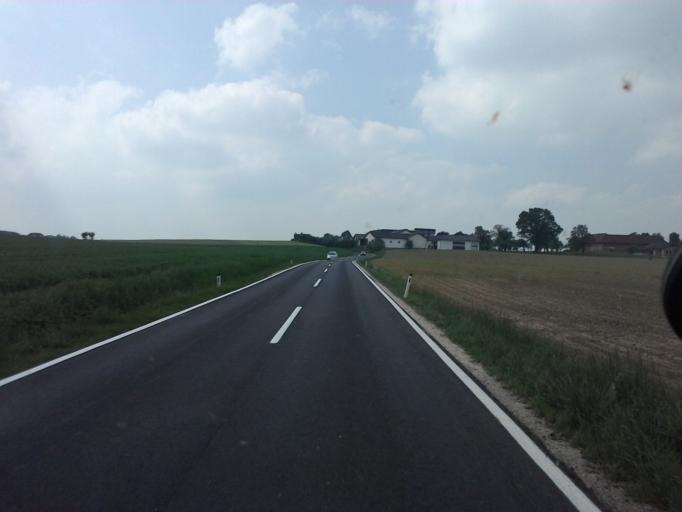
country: AT
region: Upper Austria
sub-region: Wels-Land
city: Sattledt
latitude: 48.0699
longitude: 14.0812
